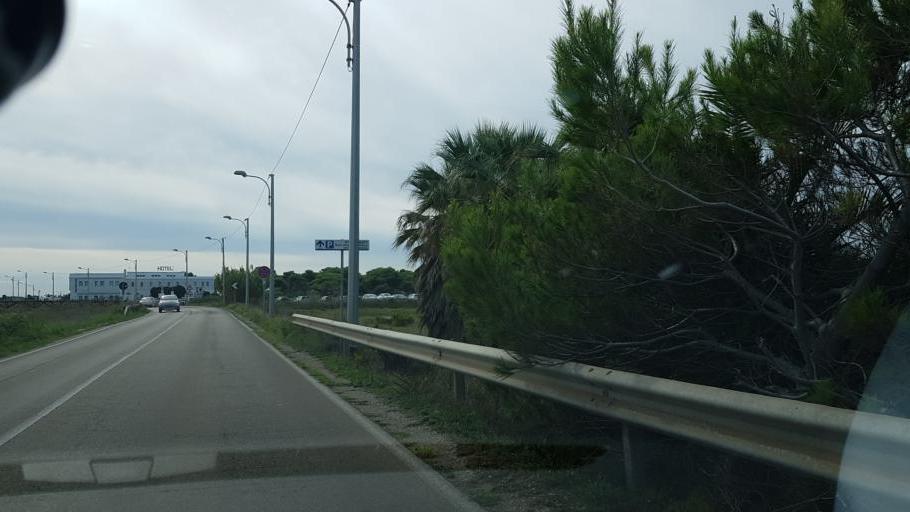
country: IT
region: Apulia
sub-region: Provincia di Lecce
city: Borgagne
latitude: 40.2885
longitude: 18.4241
